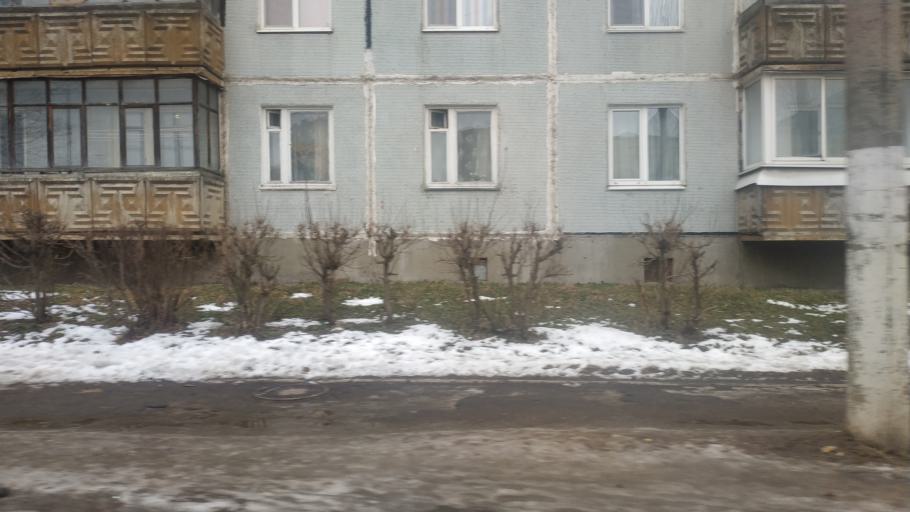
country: RU
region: Tverskaya
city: Tver
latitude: 56.8724
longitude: 35.8892
